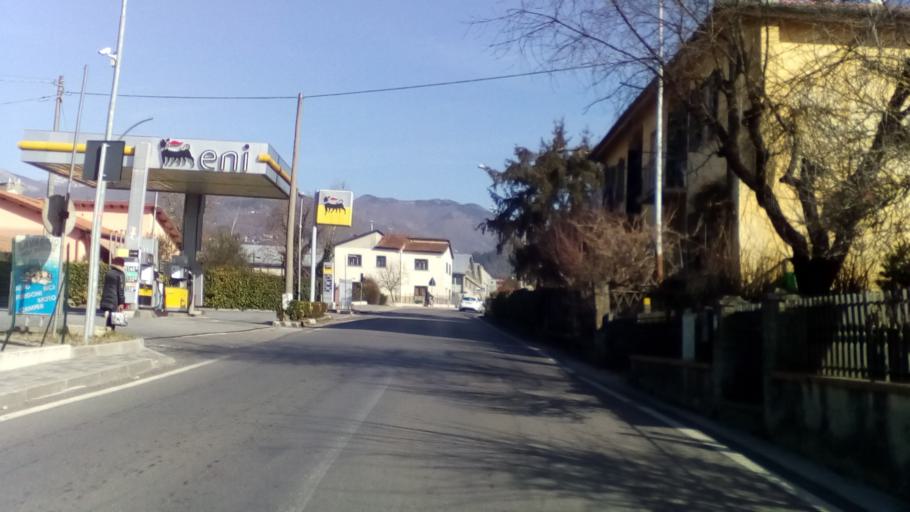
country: IT
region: Tuscany
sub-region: Provincia di Lucca
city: Pieve Fosciana
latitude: 44.1292
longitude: 10.4117
